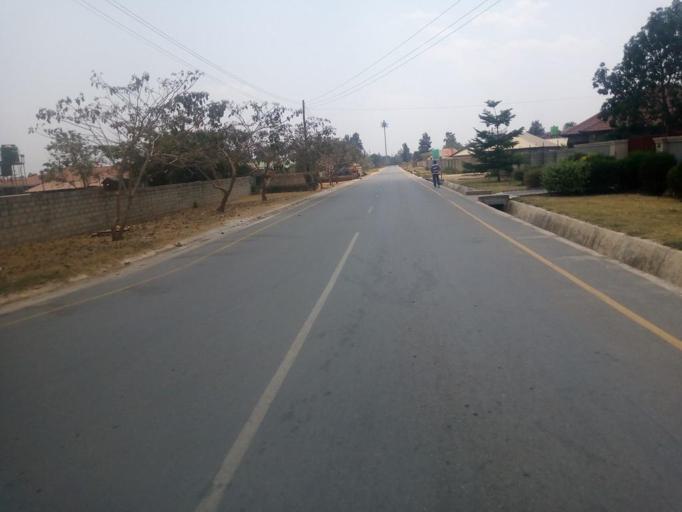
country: ZM
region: Lusaka
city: Lusaka
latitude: -15.3956
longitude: 28.3898
